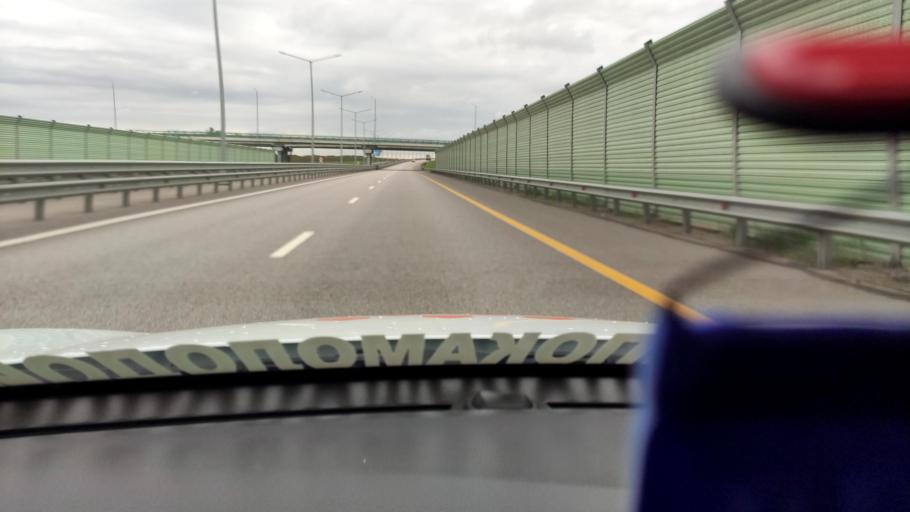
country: RU
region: Voronezj
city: Novaya Usman'
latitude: 51.6030
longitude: 39.3348
